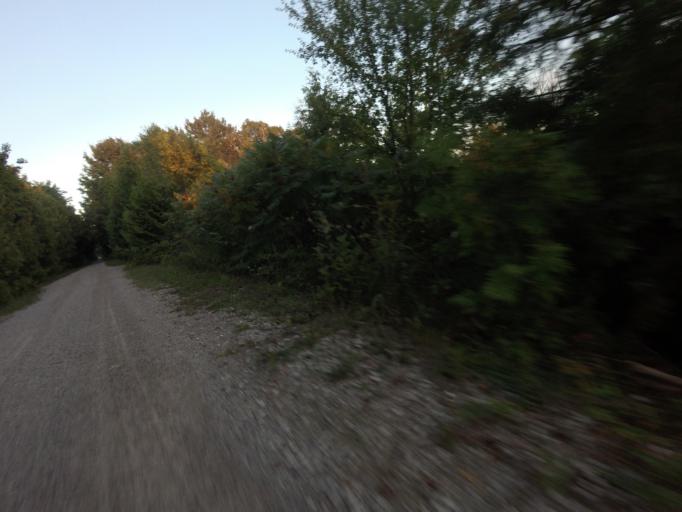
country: CA
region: Ontario
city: Goderich
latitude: 43.7525
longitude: -81.6152
